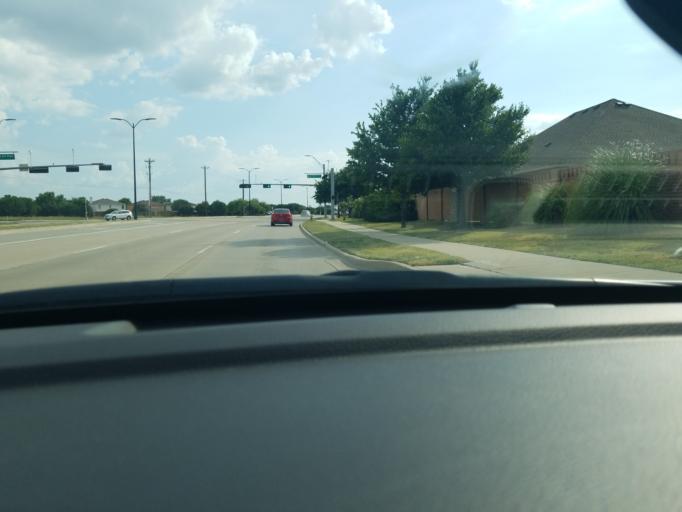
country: US
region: Texas
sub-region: Denton County
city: Little Elm
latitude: 33.1707
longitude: -96.8972
